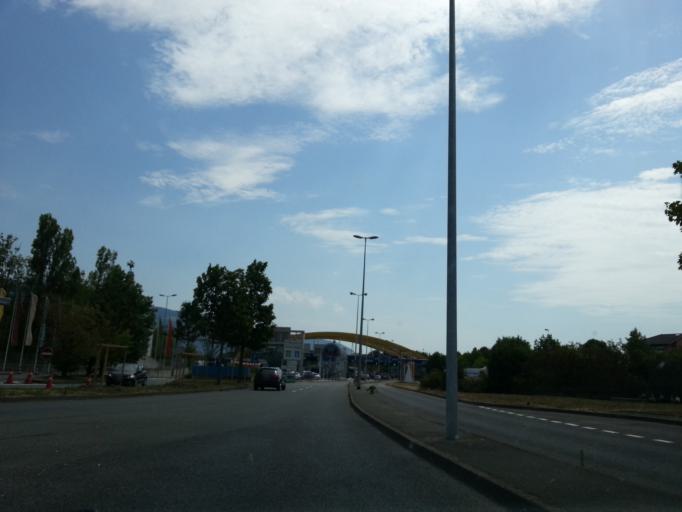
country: FR
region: Rhone-Alpes
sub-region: Departement de la Haute-Savoie
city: Saint-Julien-en-Genevois
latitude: 46.1492
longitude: 6.0953
